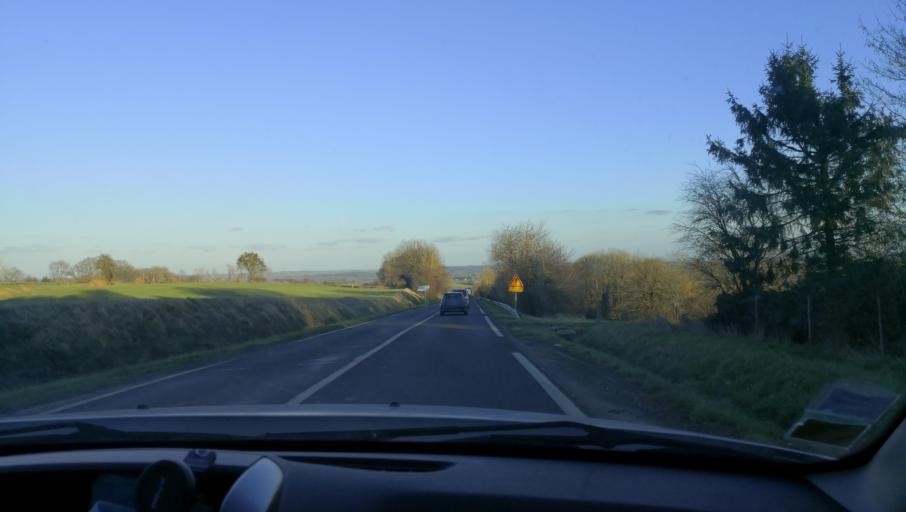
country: FR
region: Haute-Normandie
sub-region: Departement de la Seine-Maritime
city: Buchy
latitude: 49.5938
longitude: 1.4423
